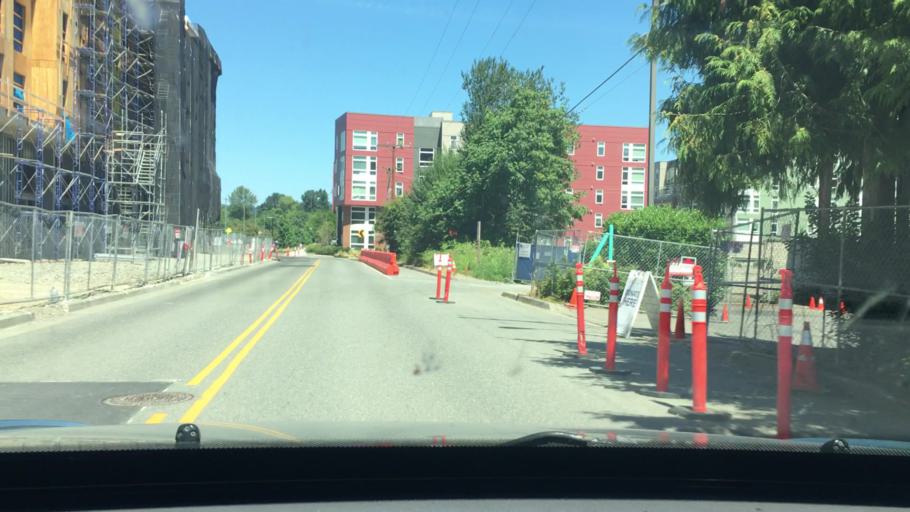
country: US
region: Washington
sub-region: King County
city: Issaquah
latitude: 47.5400
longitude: -122.0469
